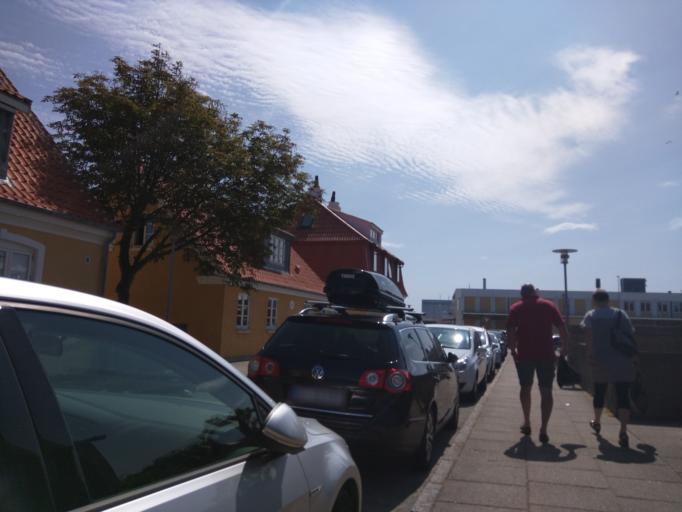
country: DK
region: North Denmark
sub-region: Frederikshavn Kommune
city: Skagen
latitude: 57.7197
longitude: 10.5856
